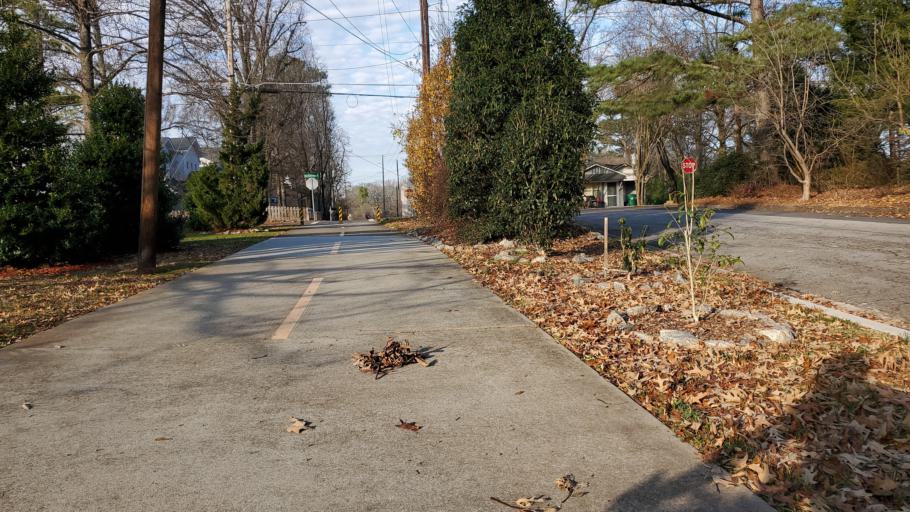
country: US
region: Georgia
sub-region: DeKalb County
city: Scottdale
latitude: 33.7809
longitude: -84.2629
